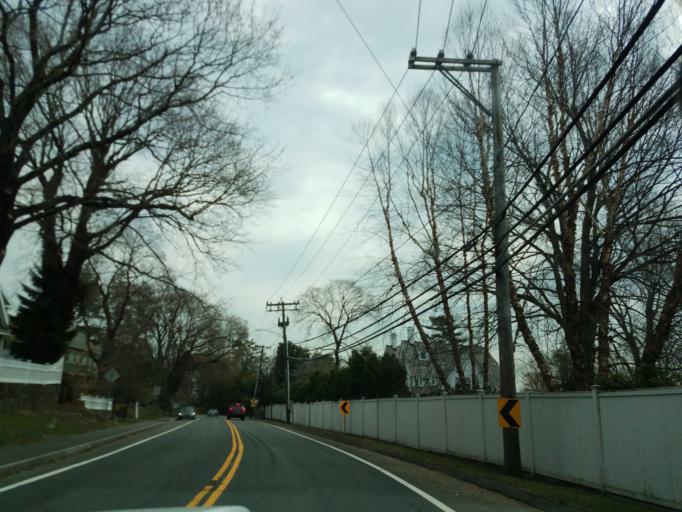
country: US
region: Connecticut
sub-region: Fairfield County
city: Greenwich
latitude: 41.0335
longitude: -73.6336
